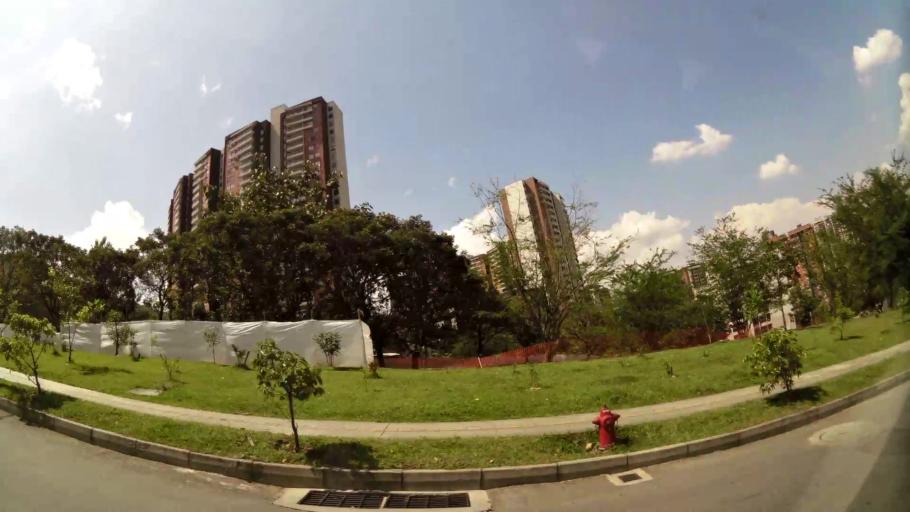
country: CO
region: Antioquia
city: Itagui
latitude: 6.2143
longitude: -75.6059
